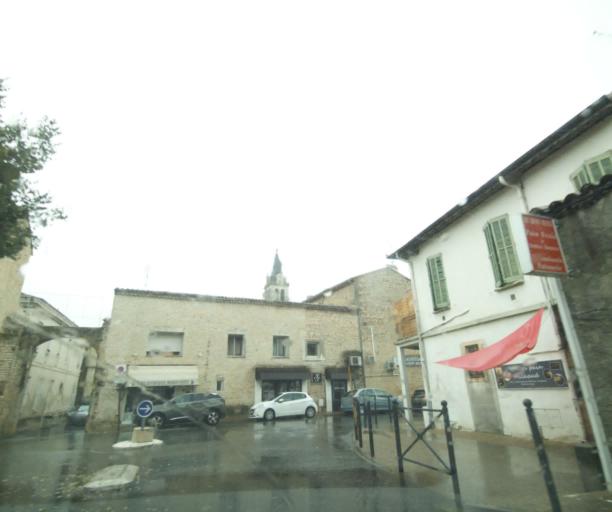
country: FR
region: Languedoc-Roussillon
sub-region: Departement du Gard
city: Milhaud
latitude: 43.7904
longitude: 4.3090
